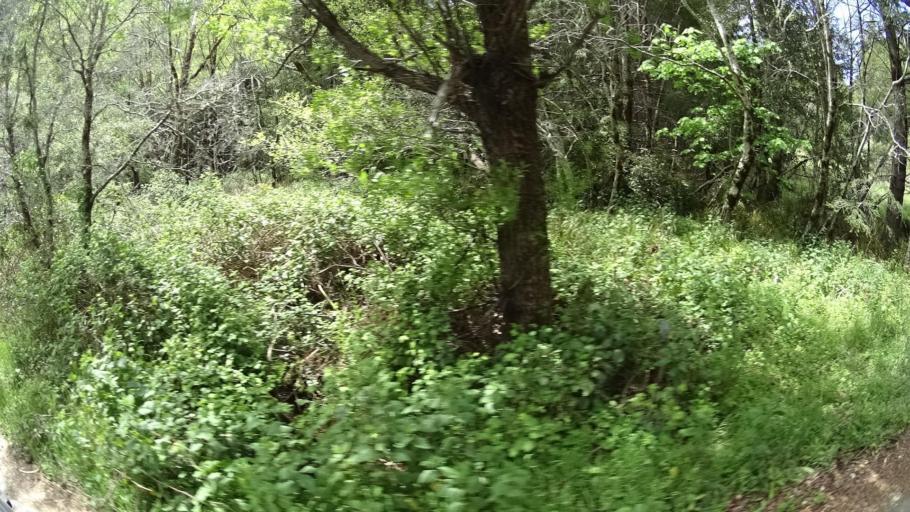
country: US
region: California
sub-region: Humboldt County
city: Redway
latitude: 40.0356
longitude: -124.0257
